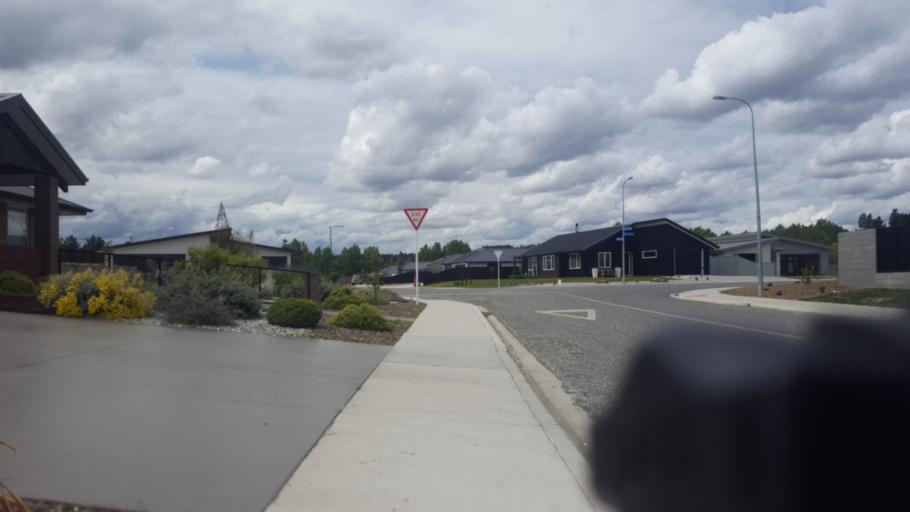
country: NZ
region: Otago
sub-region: Queenstown-Lakes District
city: Wanaka
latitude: -45.2434
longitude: 169.3744
